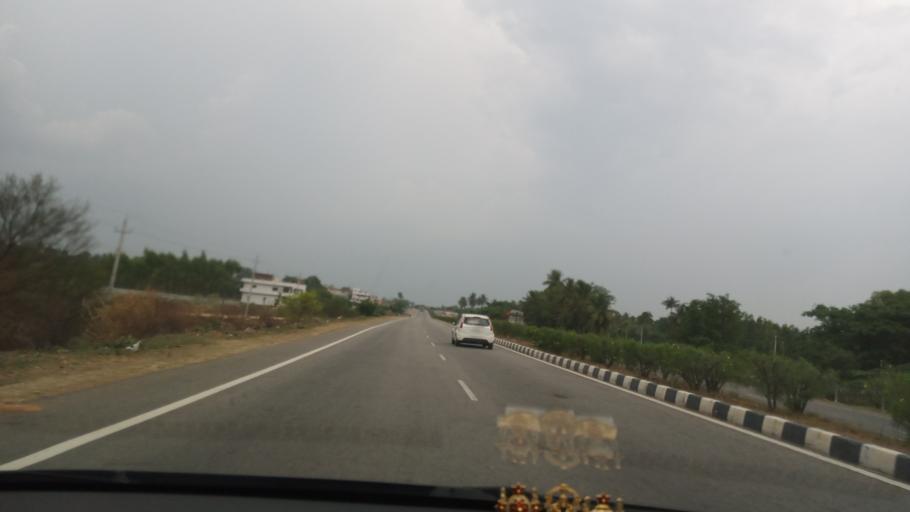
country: IN
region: Karnataka
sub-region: Kolar
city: Mulbagal
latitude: 13.2011
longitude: 78.4967
